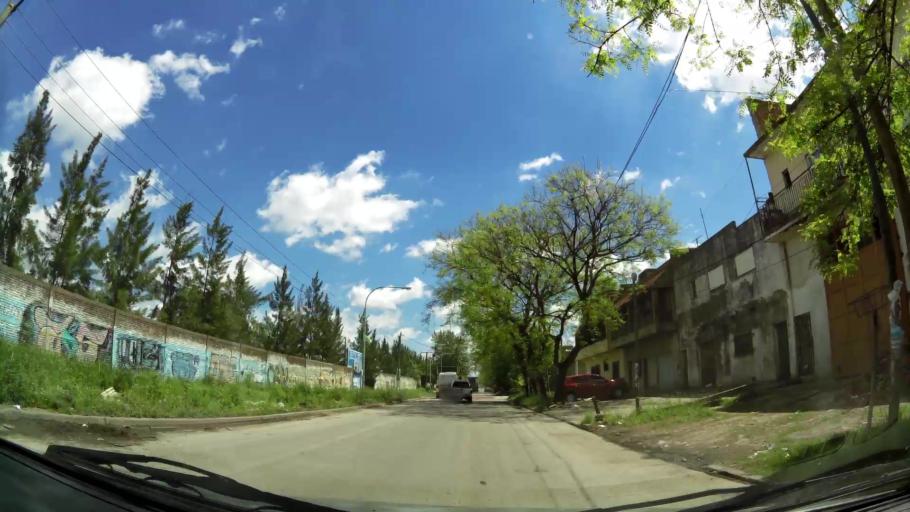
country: AR
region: Buenos Aires F.D.
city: Villa Lugano
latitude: -34.6906
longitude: -58.4361
